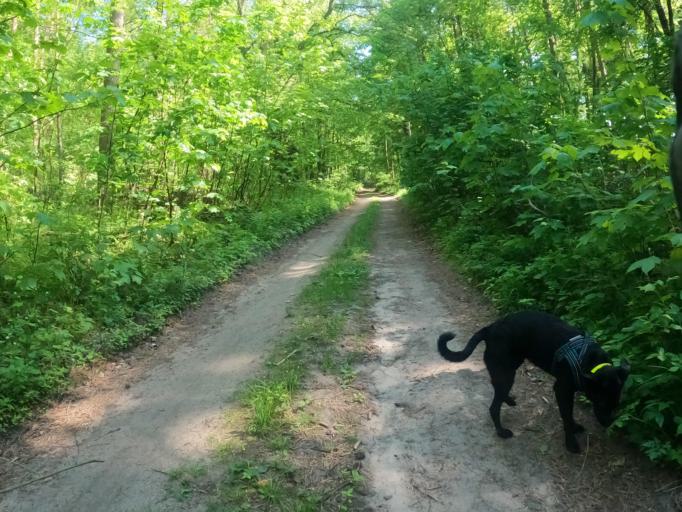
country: PL
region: West Pomeranian Voivodeship
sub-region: Powiat mysliborski
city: Barlinek
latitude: 53.0205
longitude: 15.2392
